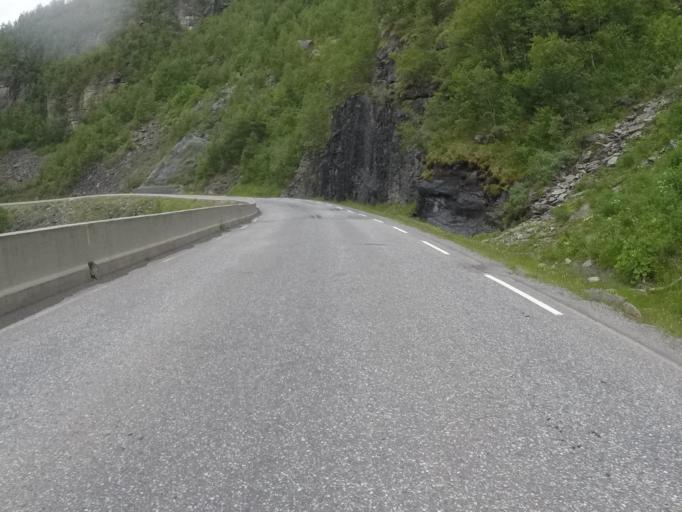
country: NO
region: Finnmark Fylke
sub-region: Alta
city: Alta
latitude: 69.7713
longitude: 23.3203
